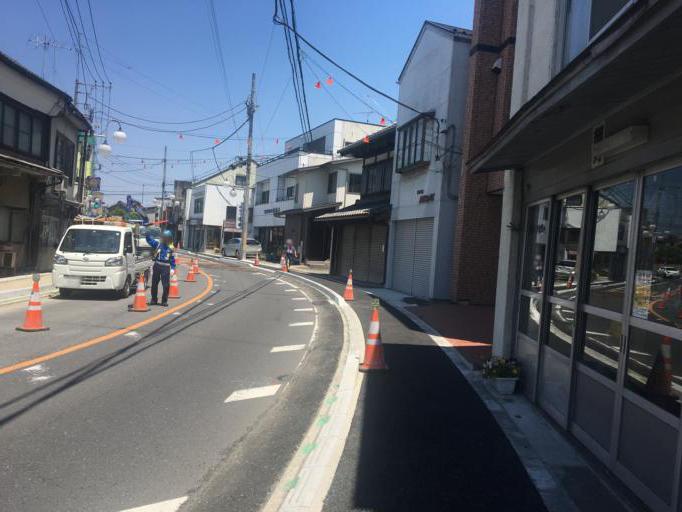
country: JP
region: Saitama
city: Ogawa
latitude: 36.0535
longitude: 139.2581
